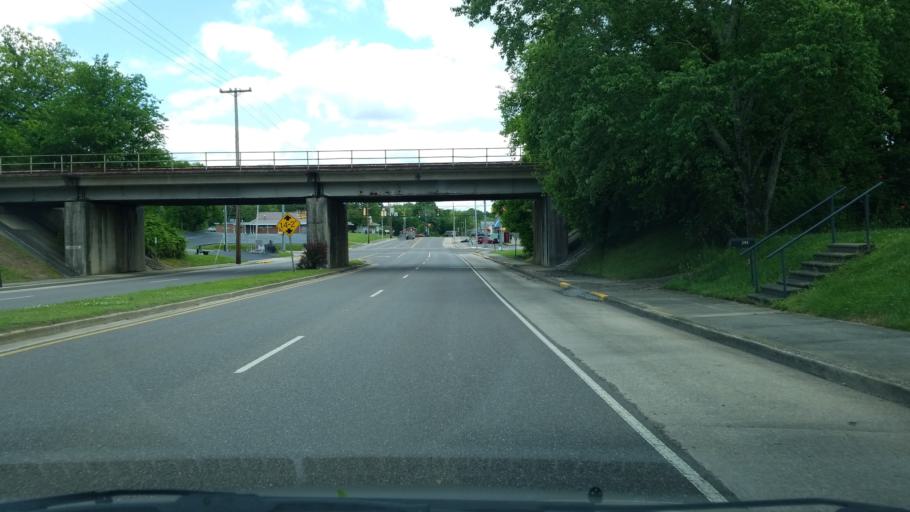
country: US
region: Tennessee
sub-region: Rhea County
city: Dayton
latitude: 35.4986
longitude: -85.0134
